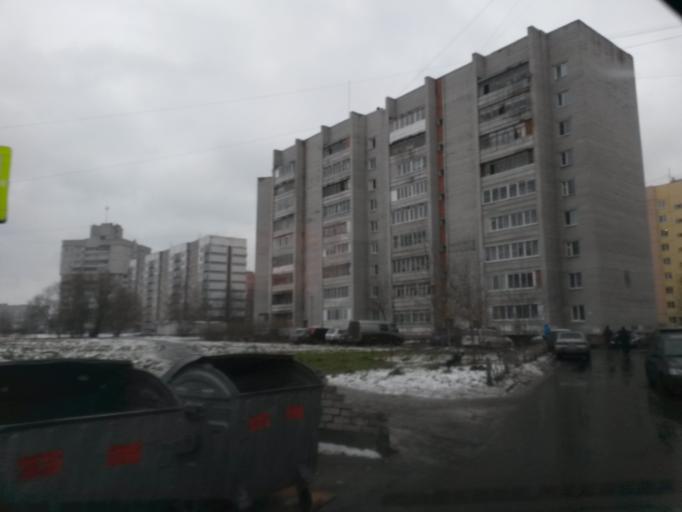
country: RU
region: Jaroslavl
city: Yaroslavl
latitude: 57.6523
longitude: 39.9589
